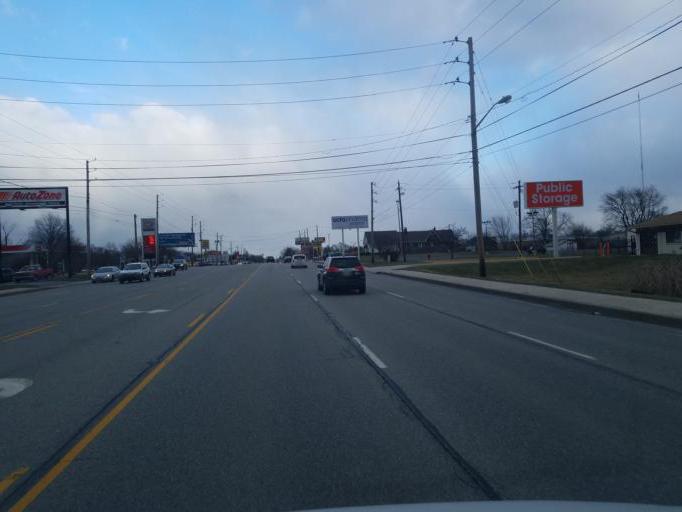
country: US
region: Indiana
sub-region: Marion County
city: Warren Park
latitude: 39.7736
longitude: -86.0150
